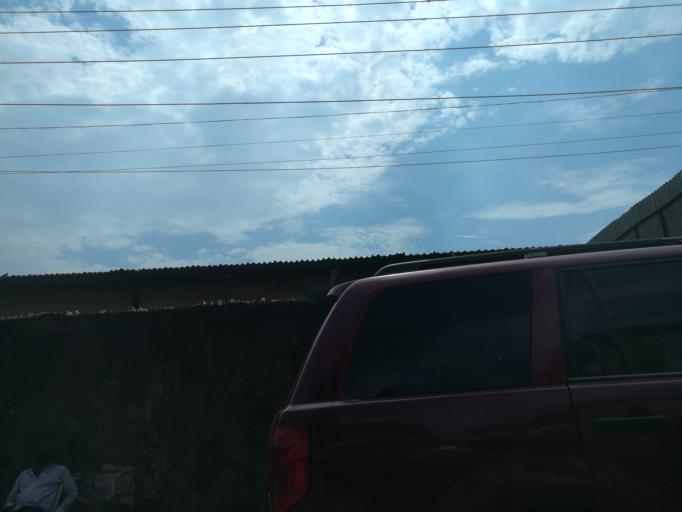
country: NG
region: Lagos
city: Oshodi
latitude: 6.5449
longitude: 3.3296
